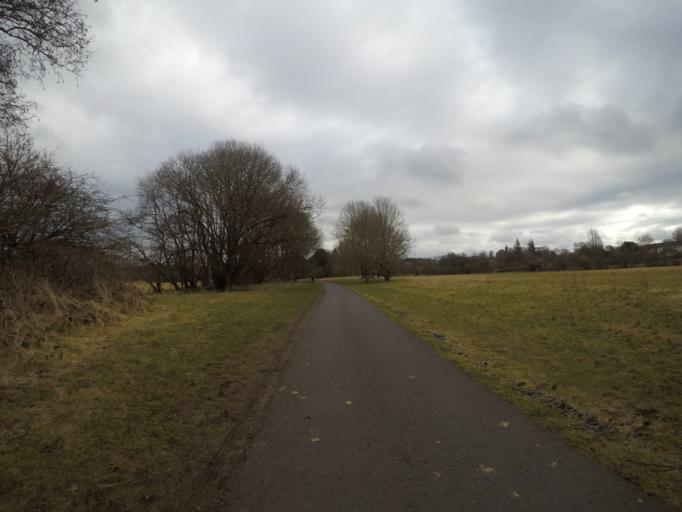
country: GB
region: Scotland
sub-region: North Ayrshire
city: Dreghorn
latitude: 55.6108
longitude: -4.6247
